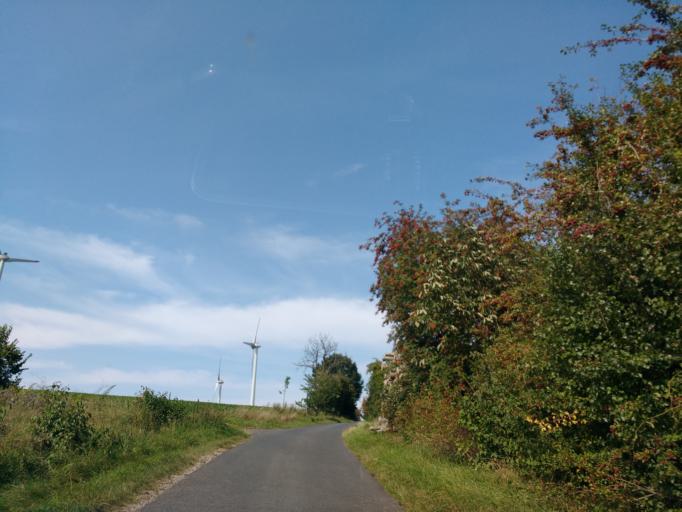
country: DE
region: Hesse
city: Witzenhausen
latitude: 51.3941
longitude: 9.8170
